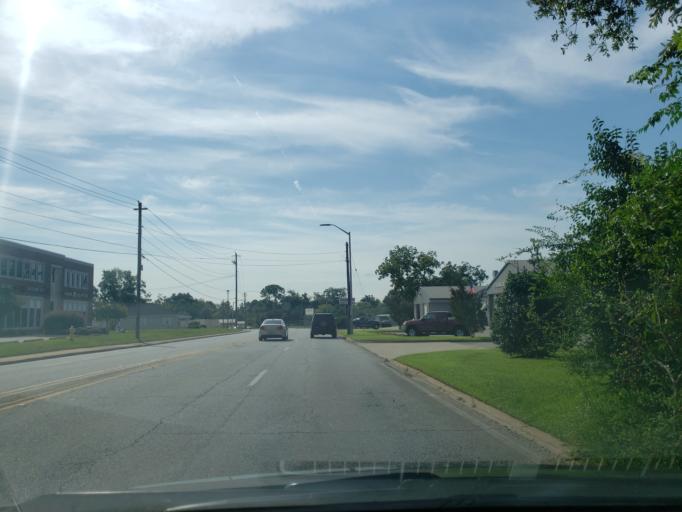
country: US
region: Georgia
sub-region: Dougherty County
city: Albany
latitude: 31.5793
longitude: -84.1726
